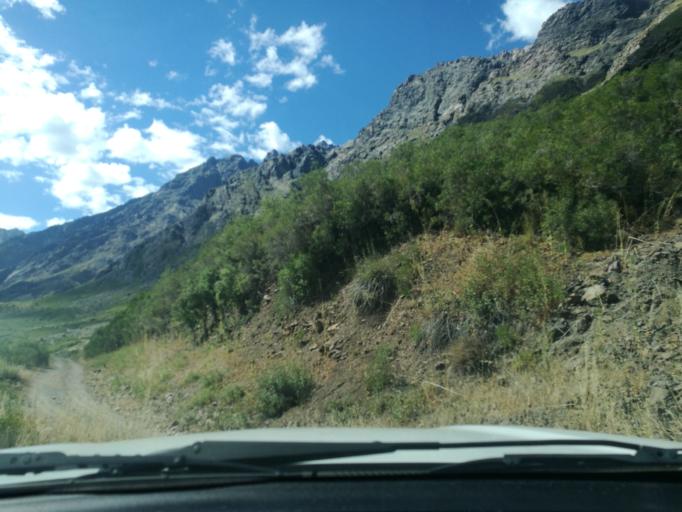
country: CL
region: O'Higgins
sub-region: Provincia de Cachapoal
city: Machali
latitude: -34.3903
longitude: -70.2778
